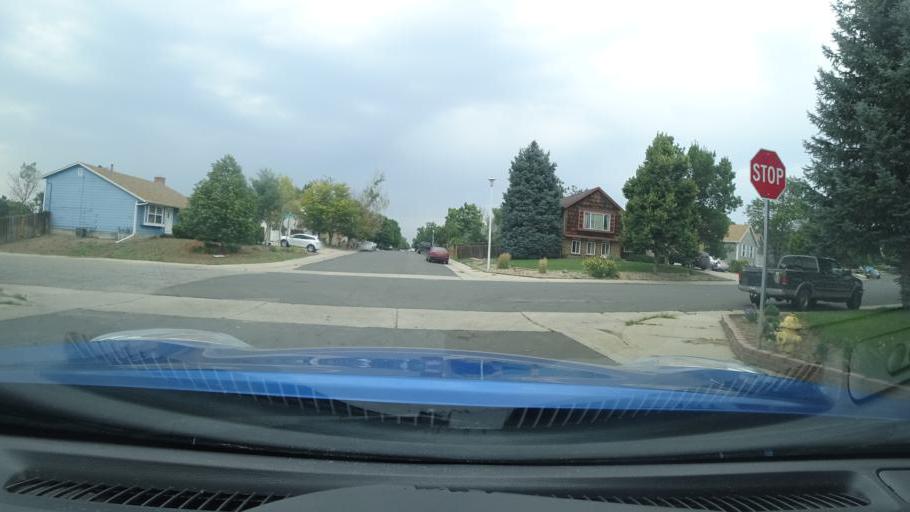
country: US
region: Colorado
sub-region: Adams County
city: Aurora
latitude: 39.6839
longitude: -104.7623
